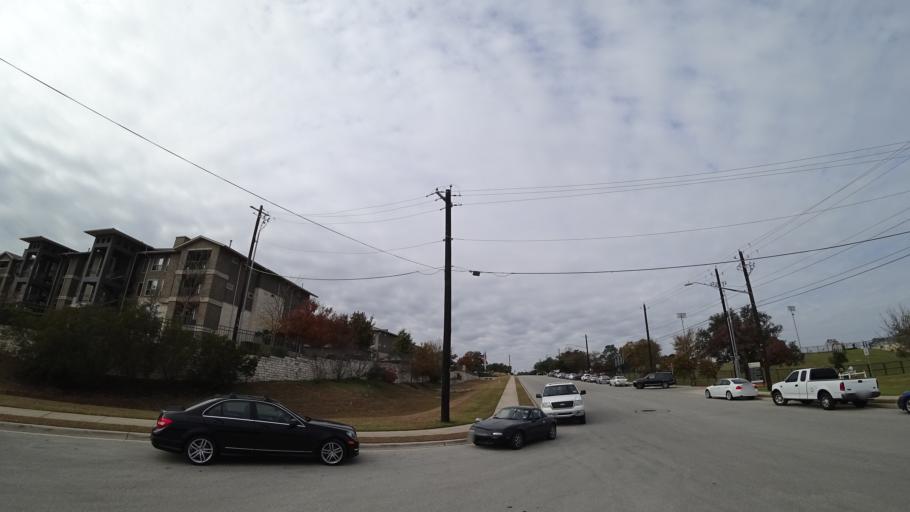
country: US
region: Texas
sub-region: Williamson County
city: Anderson Mill
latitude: 30.3952
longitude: -97.8263
